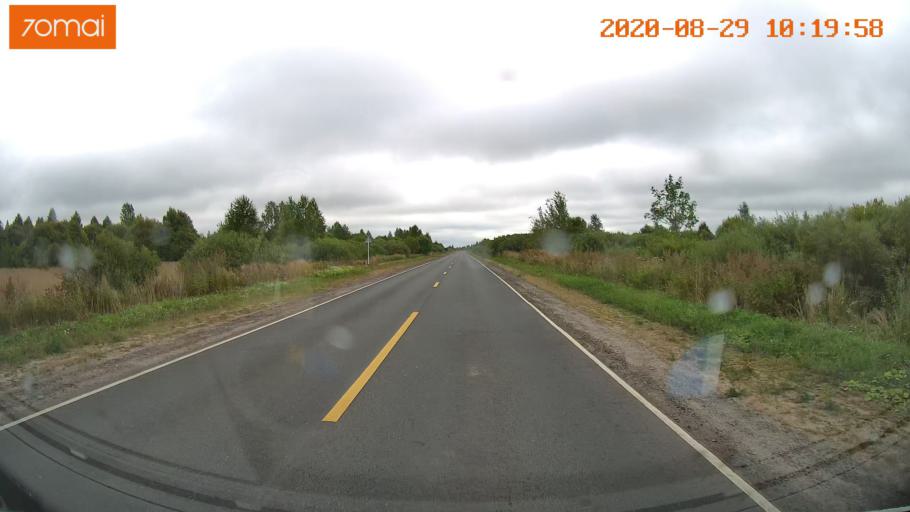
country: RU
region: Ivanovo
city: Yur'yevets
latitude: 57.3257
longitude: 42.8728
